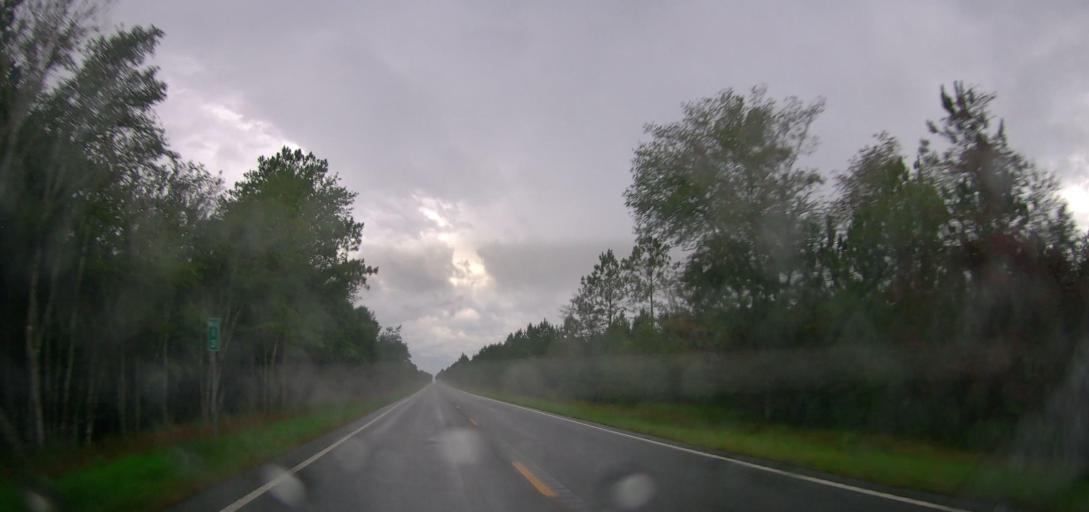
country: US
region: Georgia
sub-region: Brantley County
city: Nahunta
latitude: 31.3427
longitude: -81.8191
